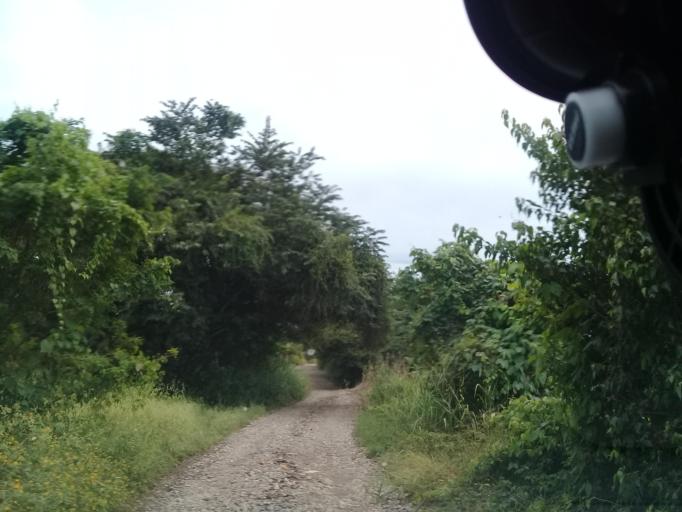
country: MX
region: Hidalgo
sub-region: Huejutla de Reyes
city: Parque de Poblamiento Solidaridad
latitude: 21.1741
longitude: -98.3762
